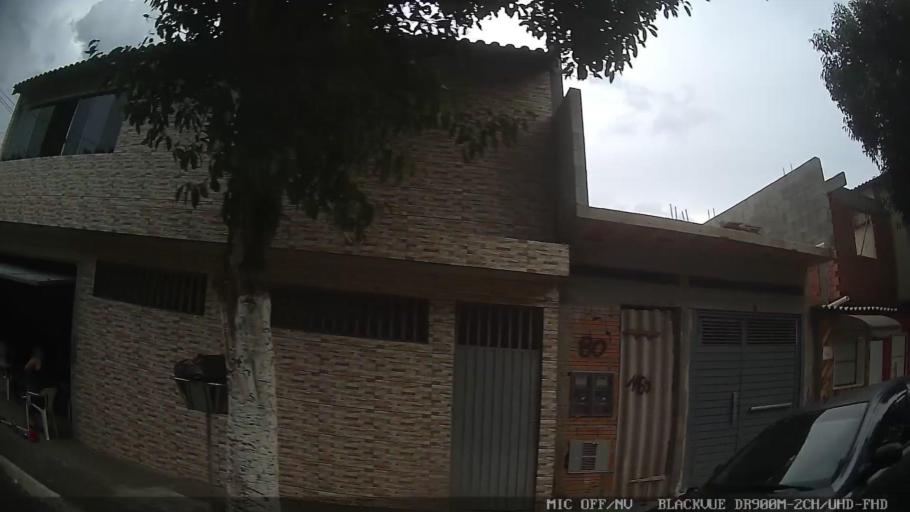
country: BR
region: Sao Paulo
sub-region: Suzano
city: Suzano
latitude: -23.5616
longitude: -46.2928
